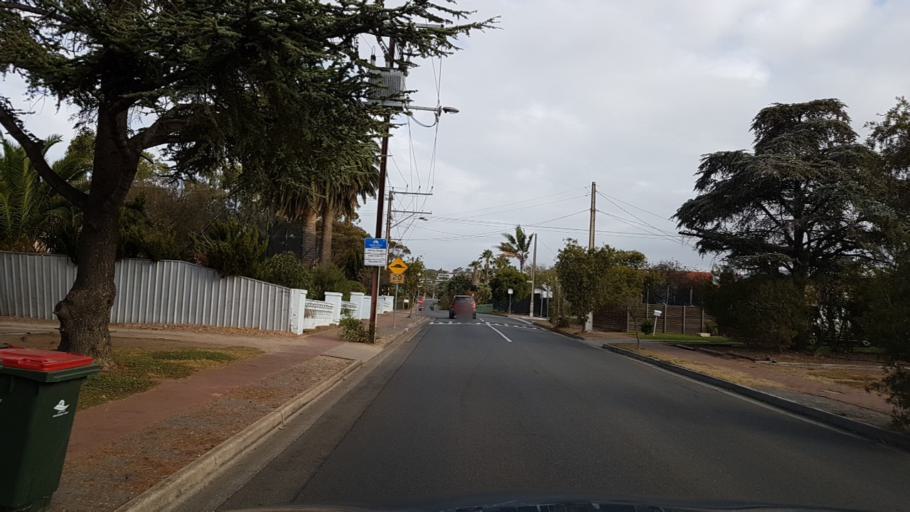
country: AU
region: South Australia
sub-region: Adelaide Hills
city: Seacliff
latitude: -35.0357
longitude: 138.5216
